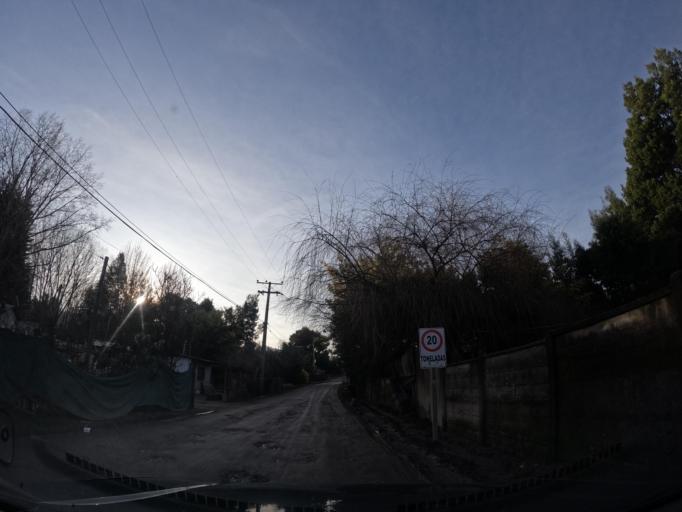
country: CL
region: Biobio
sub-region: Provincia de Concepcion
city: Concepcion
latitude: -36.8535
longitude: -73.0054
